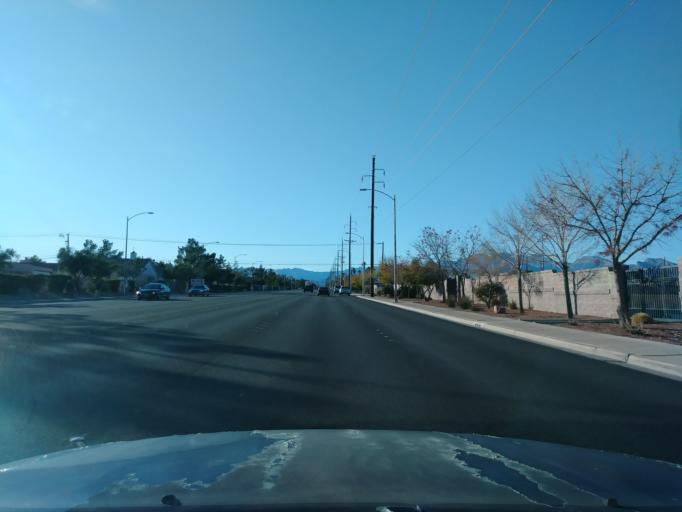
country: US
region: Nevada
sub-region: Clark County
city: Spring Valley
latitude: 36.1592
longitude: -115.2576
